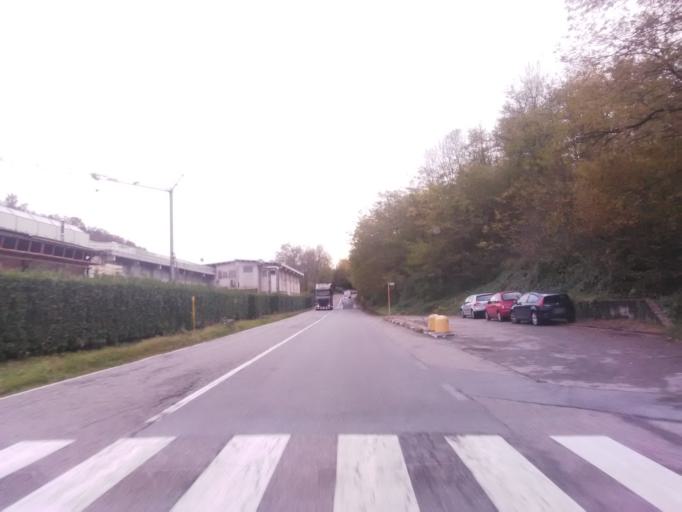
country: IT
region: Piedmont
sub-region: Provincia di Vercelli
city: Borgosesia
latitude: 45.7138
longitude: 8.2976
